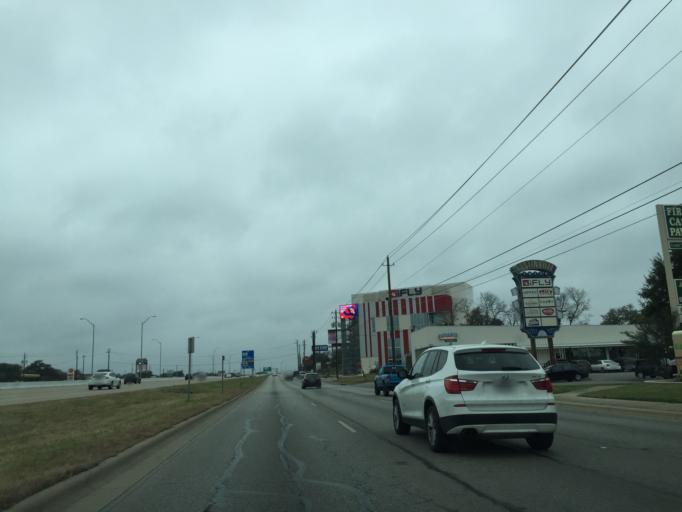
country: US
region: Texas
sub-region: Williamson County
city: Jollyville
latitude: 30.4427
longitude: -97.7837
